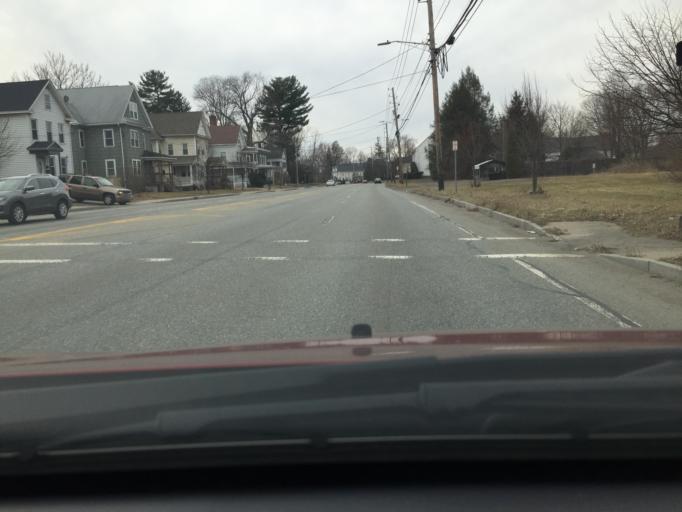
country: US
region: Massachusetts
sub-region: Hampden County
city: Westfield
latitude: 42.1182
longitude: -72.7364
